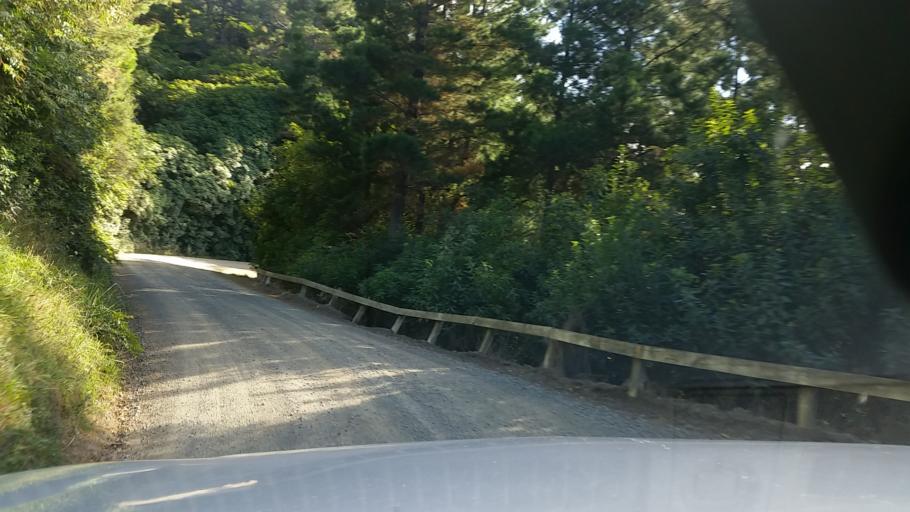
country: NZ
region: Marlborough
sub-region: Marlborough District
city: Picton
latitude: -41.2966
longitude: 174.1237
